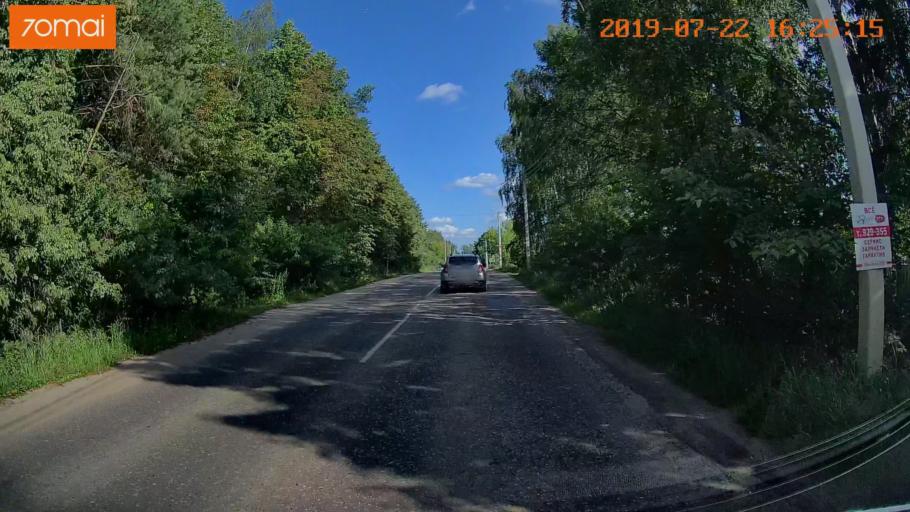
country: RU
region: Ivanovo
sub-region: Gorod Ivanovo
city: Ivanovo
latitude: 57.0545
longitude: 40.9232
